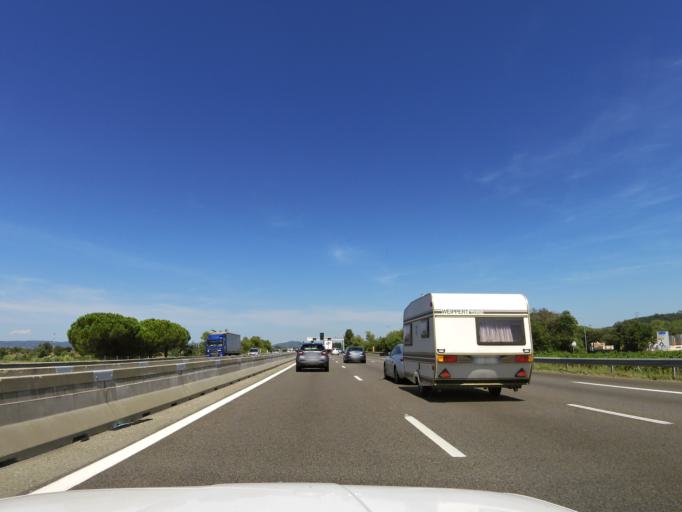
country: FR
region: Rhone-Alpes
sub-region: Departement de la Drome
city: Saint-Paul-Trois-Chateaux
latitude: 44.3513
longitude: 4.7379
